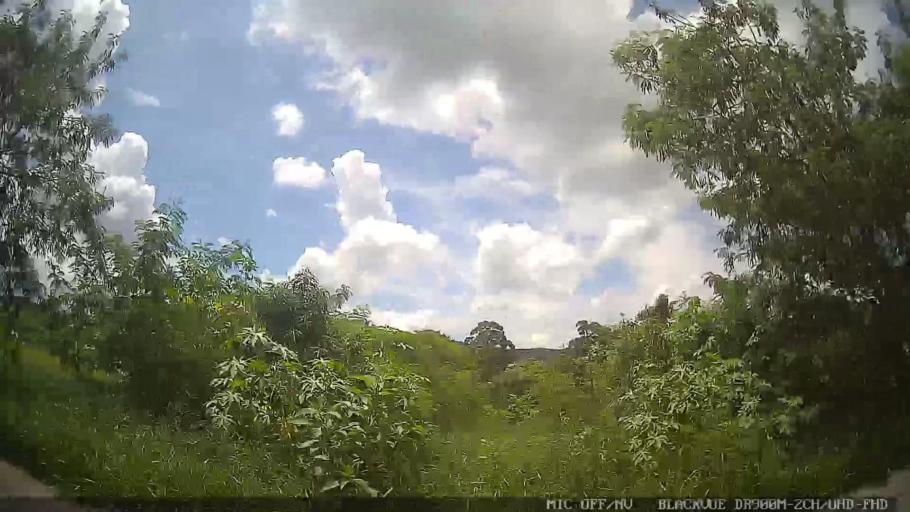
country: BR
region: Sao Paulo
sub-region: Mogi das Cruzes
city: Mogi das Cruzes
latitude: -23.5083
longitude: -46.1898
